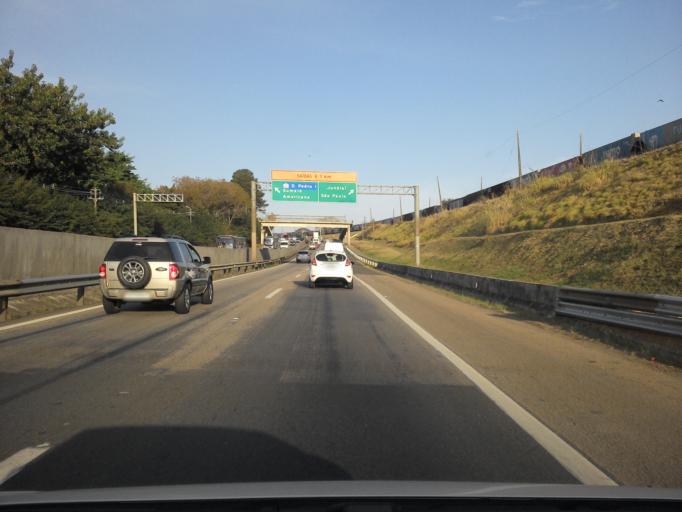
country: BR
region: Sao Paulo
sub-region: Campinas
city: Campinas
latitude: -22.8974
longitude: -47.1214
